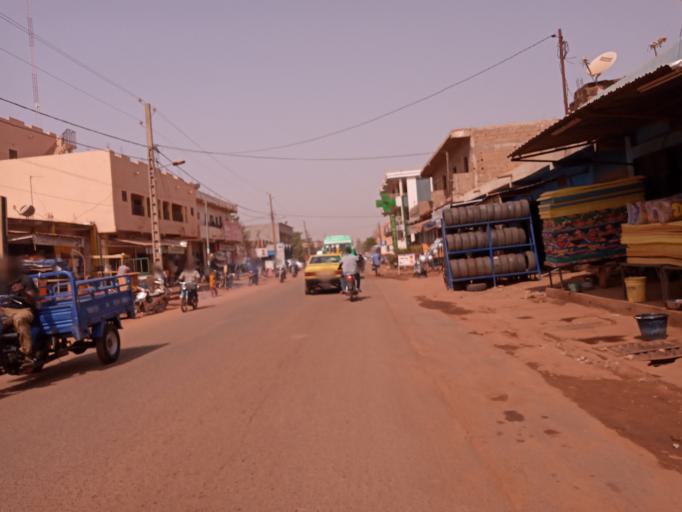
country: ML
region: Bamako
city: Bamako
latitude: 12.5884
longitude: -7.9702
